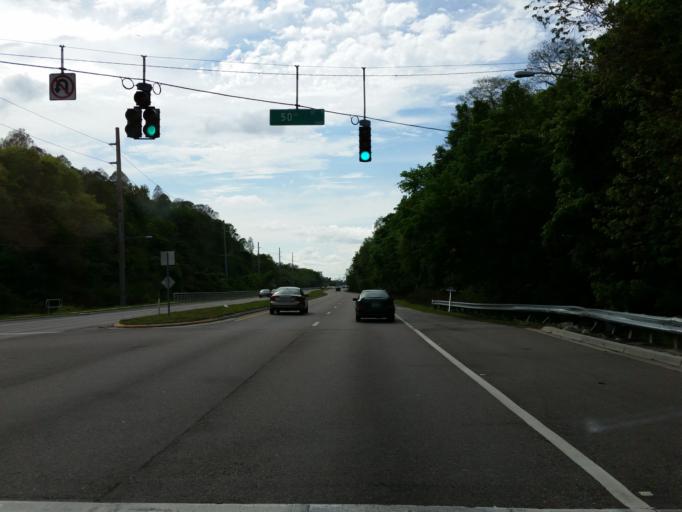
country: US
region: Florida
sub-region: Hillsborough County
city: University
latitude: 28.0693
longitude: -82.4017
